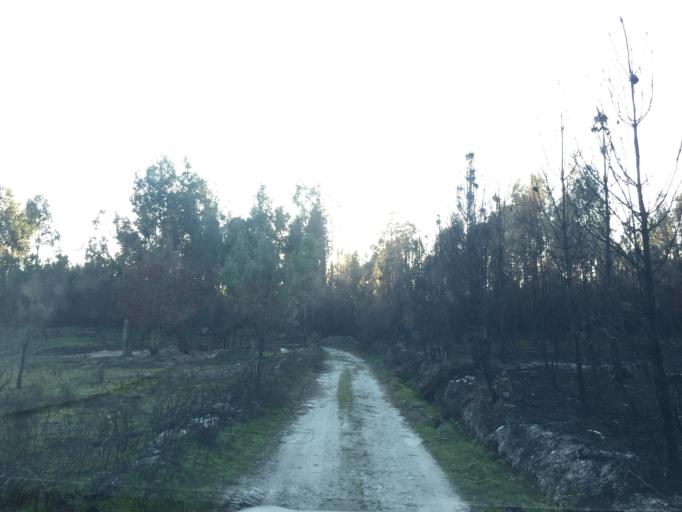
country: PT
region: Viseu
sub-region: Concelho de Carregal do Sal
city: Carregal do Sal
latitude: 40.4630
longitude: -7.9279
